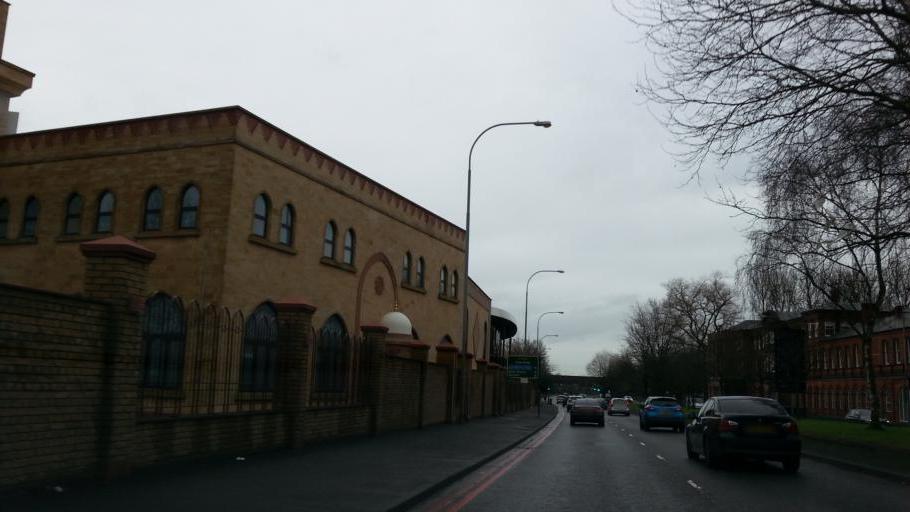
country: GB
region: England
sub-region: City and Borough of Birmingham
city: Hockley
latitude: 52.4875
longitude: -1.9177
